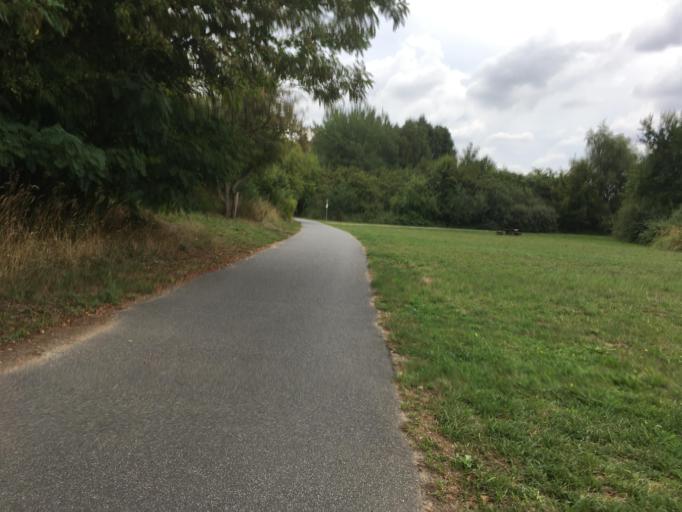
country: DE
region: Brandenburg
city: Prenzlau
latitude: 53.2929
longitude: 13.8691
